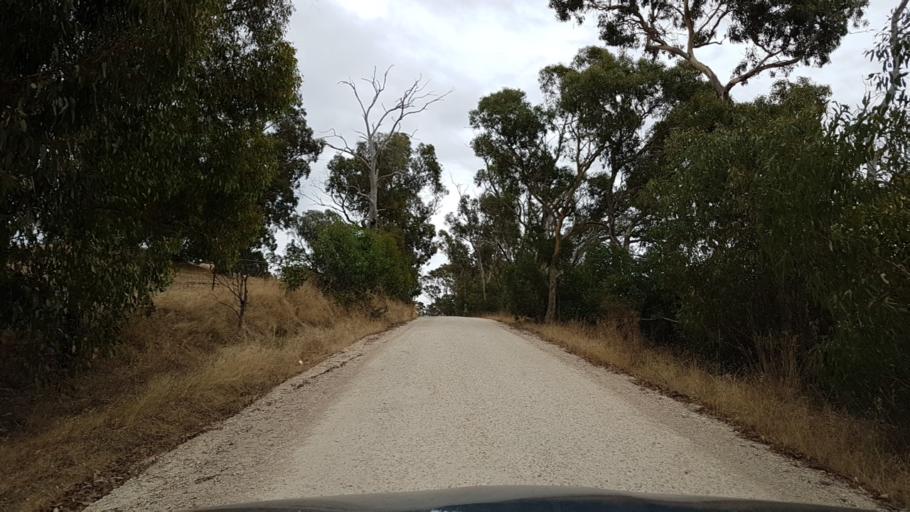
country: AU
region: South Australia
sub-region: Adelaide Hills
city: Gumeracha
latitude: -34.7969
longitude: 138.8174
